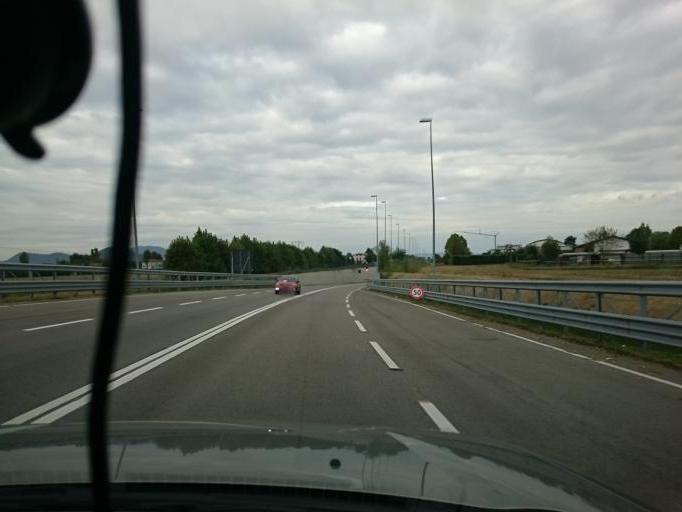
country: IT
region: Veneto
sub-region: Provincia di Padova
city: Selvazzano Dentro
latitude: 45.3773
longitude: 11.8010
